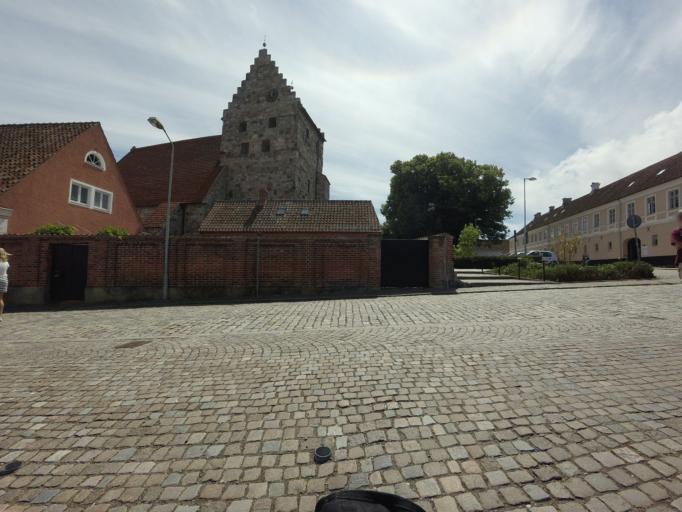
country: SE
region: Skane
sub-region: Simrishamns Kommun
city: Simrishamn
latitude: 55.5572
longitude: 14.3483
